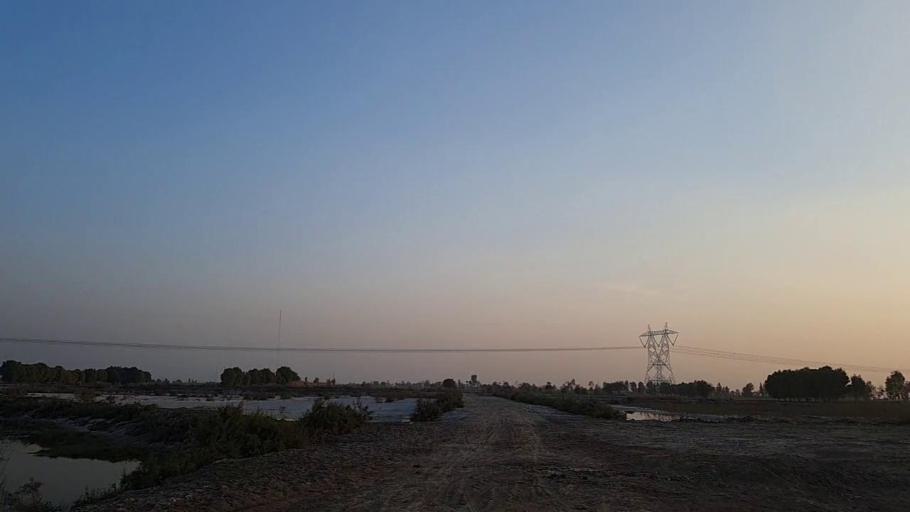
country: PK
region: Sindh
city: Naushahro Firoz
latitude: 26.7785
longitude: 68.0718
